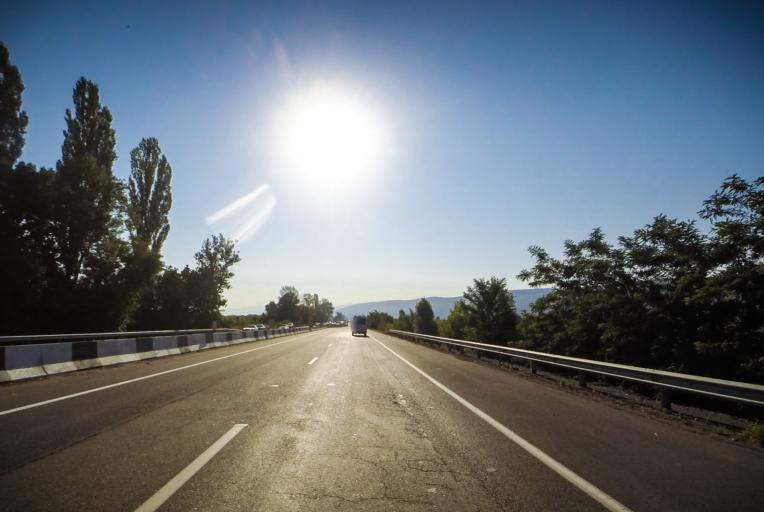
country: RU
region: North Ossetia
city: Zmeyskaya
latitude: 43.3230
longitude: 44.1257
